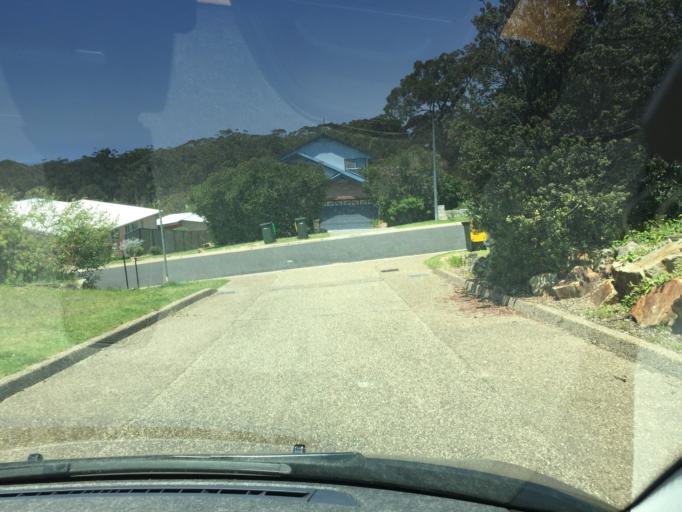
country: AU
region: New South Wales
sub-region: Bega Valley
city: Merimbula
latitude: -36.8536
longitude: 149.9303
